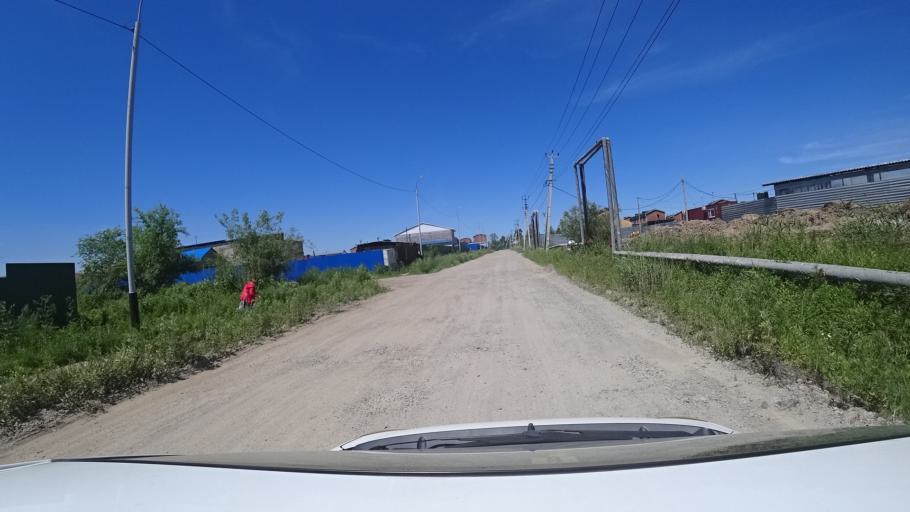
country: RU
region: Khabarovsk Krai
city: Topolevo
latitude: 48.5029
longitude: 135.1822
